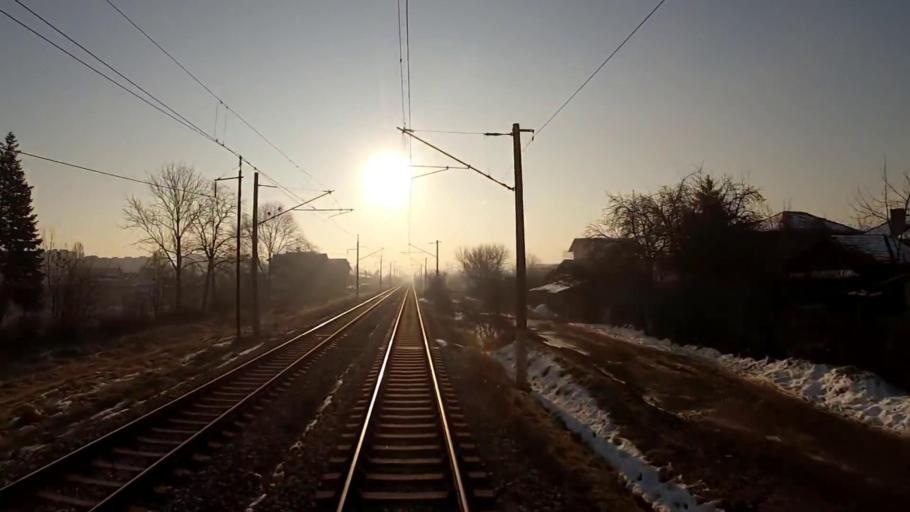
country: BG
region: Sofia-Capital
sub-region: Stolichna Obshtina
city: Sofia
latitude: 42.7339
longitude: 23.2691
